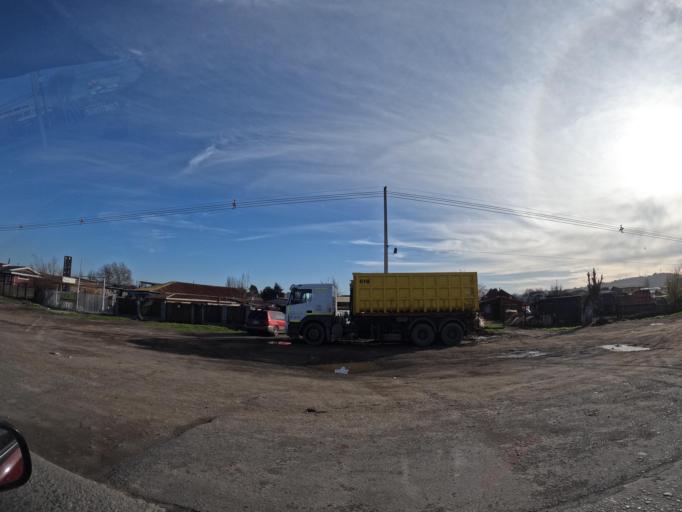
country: CL
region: Biobio
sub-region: Provincia de Concepcion
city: Concepcion
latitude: -36.7759
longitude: -73.0795
